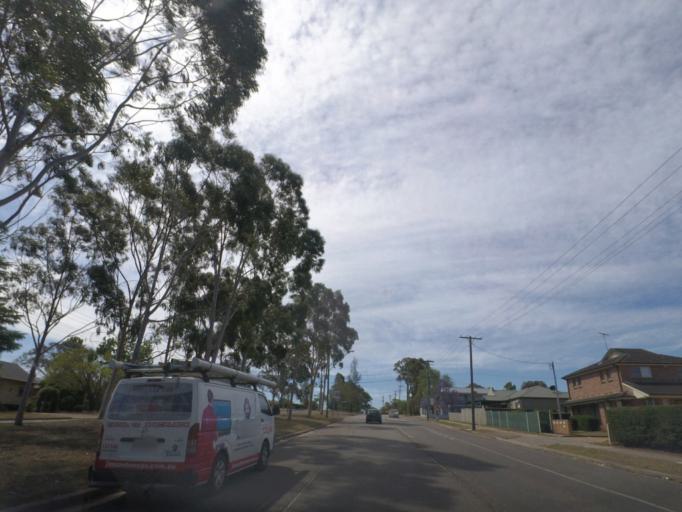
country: AU
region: New South Wales
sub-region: Camden
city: Camden South
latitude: -34.0689
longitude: 150.6941
